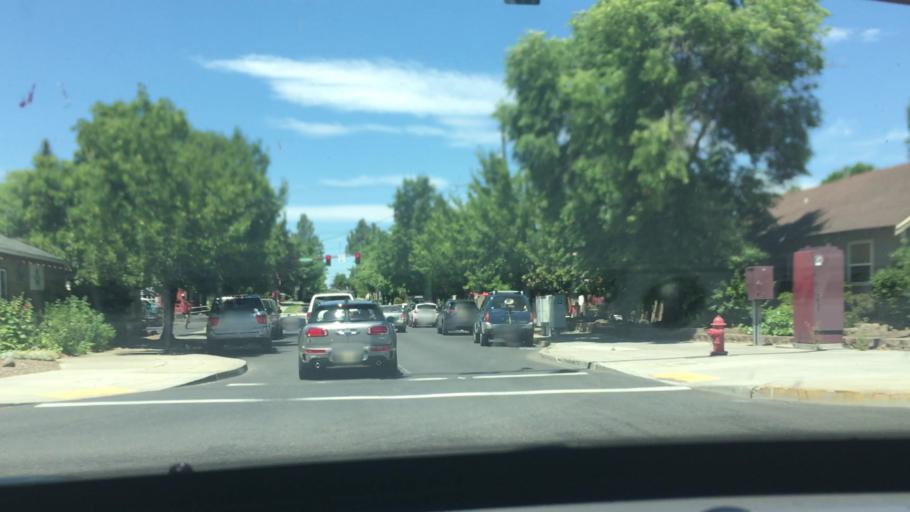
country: US
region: Oregon
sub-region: Deschutes County
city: Bend
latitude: 44.0515
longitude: -121.3165
